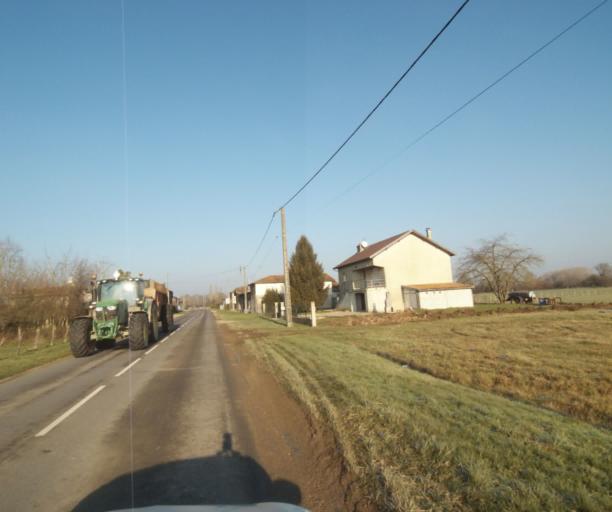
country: FR
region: Champagne-Ardenne
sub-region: Departement de la Haute-Marne
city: Montier-en-Der
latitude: 48.4588
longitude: 4.7689
